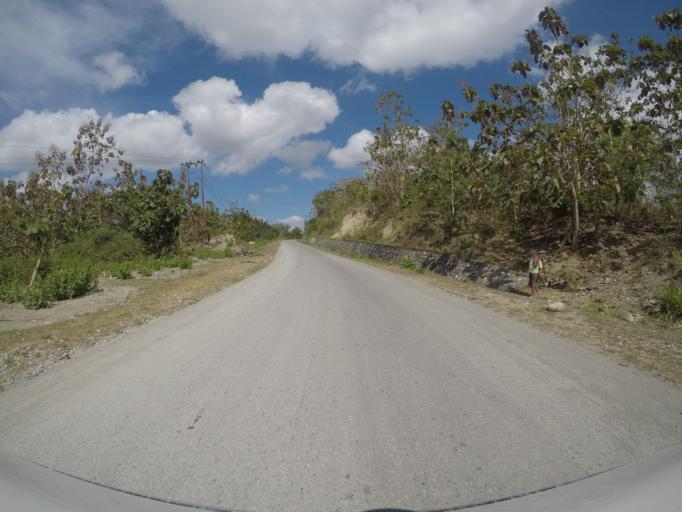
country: TL
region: Viqueque
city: Viqueque
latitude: -8.8712
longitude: 126.3536
